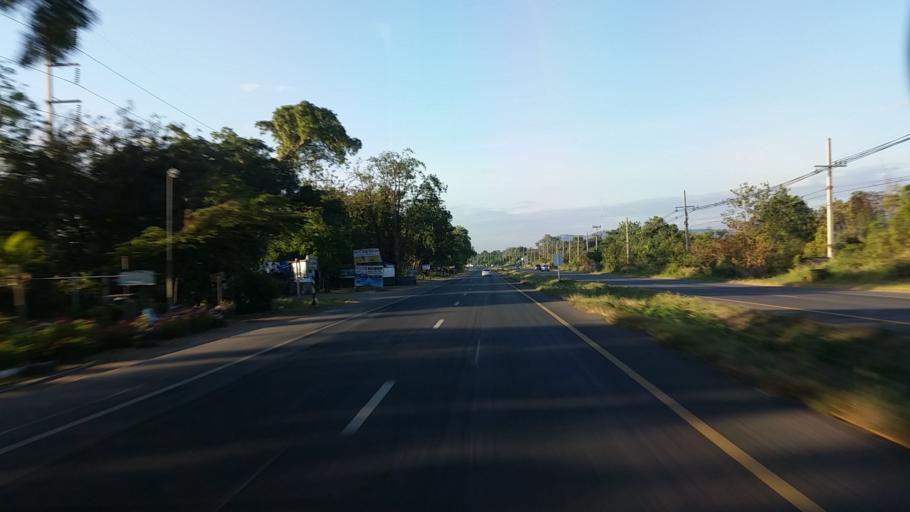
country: TH
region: Lop Buri
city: Chai Badan
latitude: 15.1832
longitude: 101.0738
